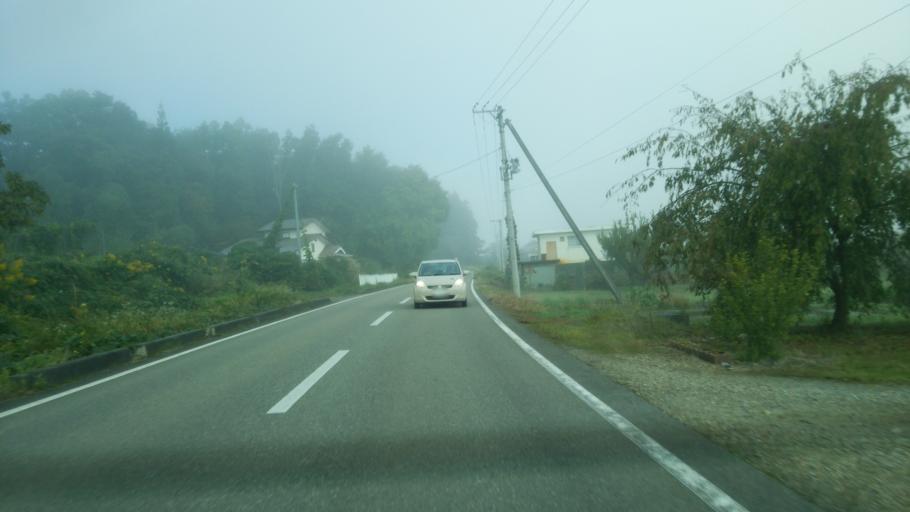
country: JP
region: Fukushima
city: Kitakata
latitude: 37.5124
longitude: 139.8222
